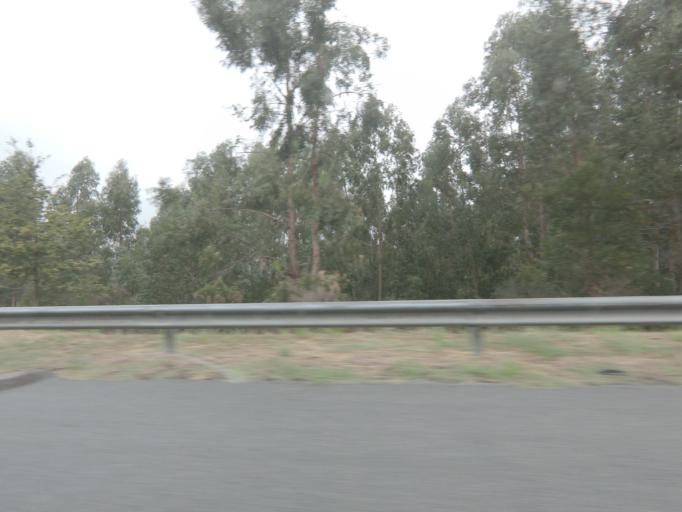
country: PT
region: Porto
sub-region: Penafiel
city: Penafiel
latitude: 41.2181
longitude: -8.2685
